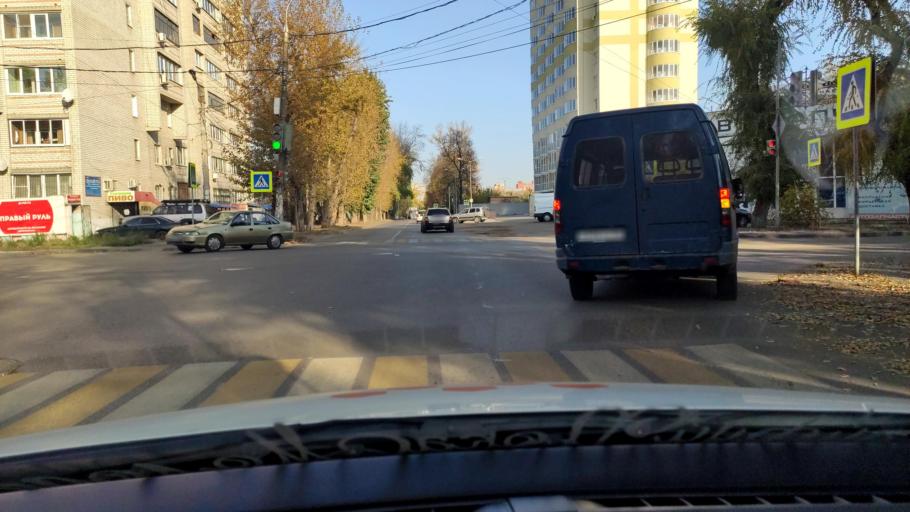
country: RU
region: Voronezj
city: Voronezh
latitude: 51.6870
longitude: 39.1908
